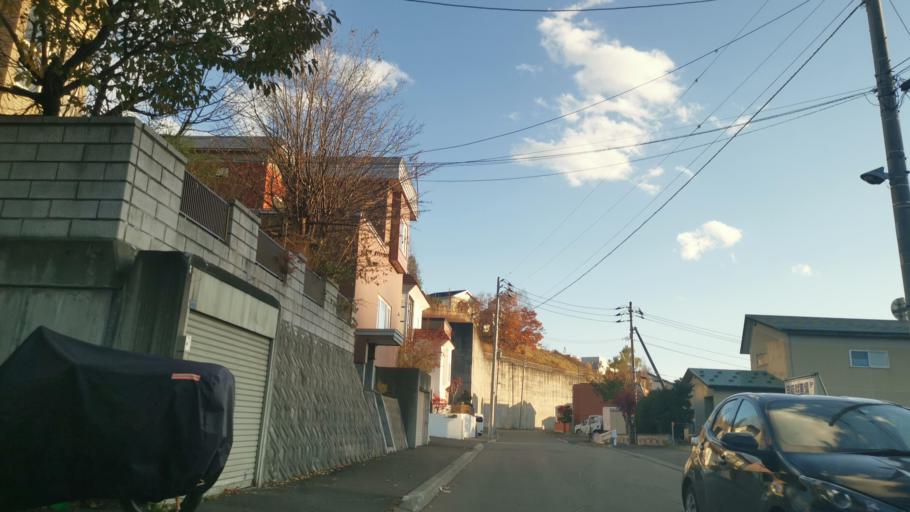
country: JP
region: Hokkaido
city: Sapporo
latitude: 42.9977
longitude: 141.3657
